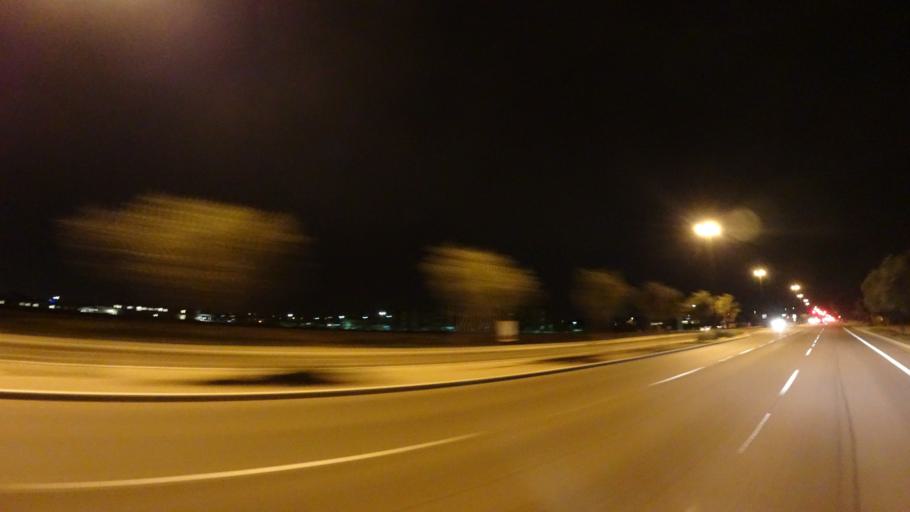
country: US
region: Arizona
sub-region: Maricopa County
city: Gilbert
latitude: 33.3752
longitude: -111.7224
